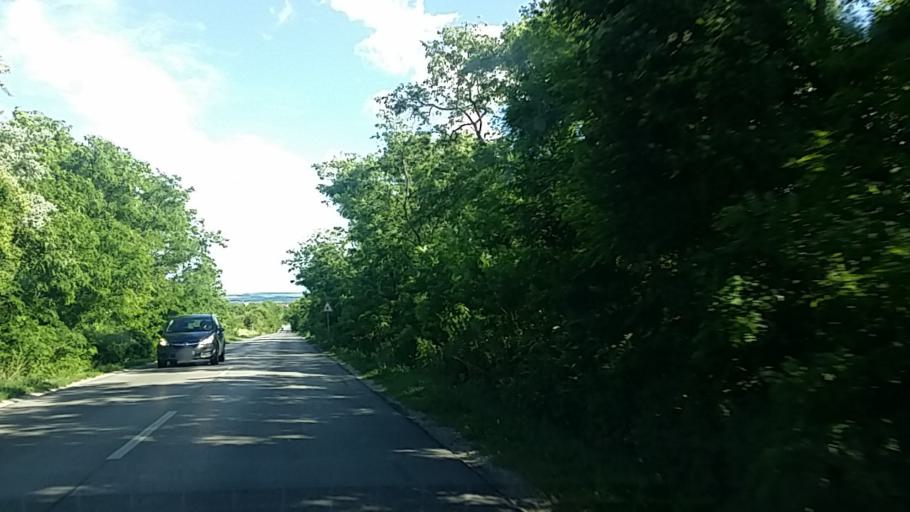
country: HU
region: Pest
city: Zsambek
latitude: 47.5531
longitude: 18.6967
